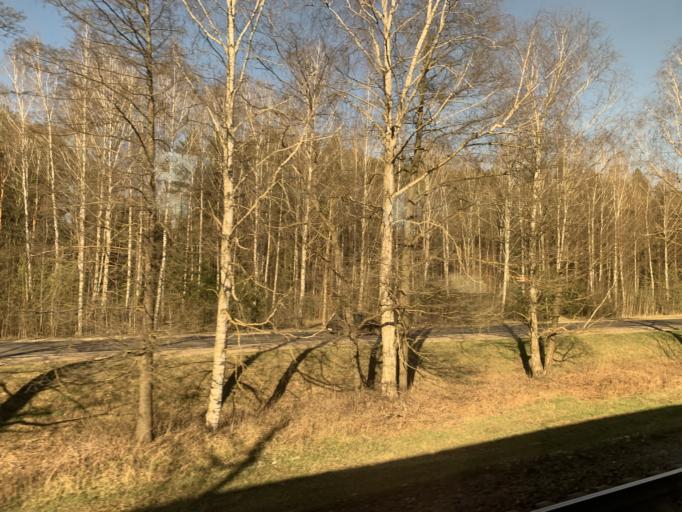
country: BY
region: Grodnenskaya
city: Smarhon'
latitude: 54.4416
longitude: 26.5017
